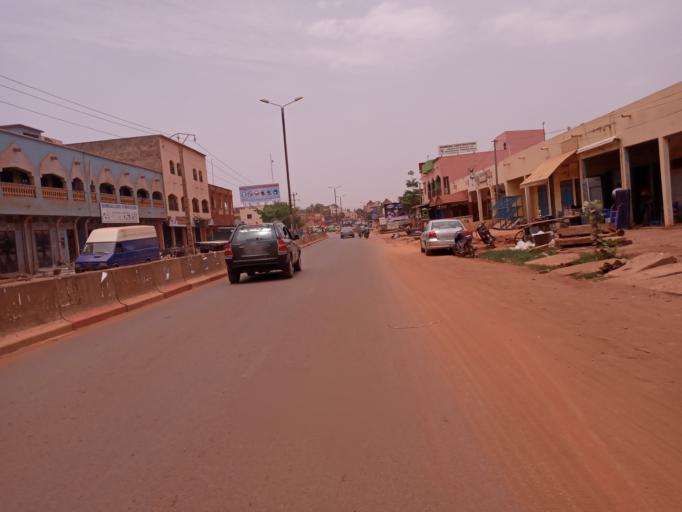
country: ML
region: Bamako
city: Bamako
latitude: 12.5854
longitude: -8.0227
